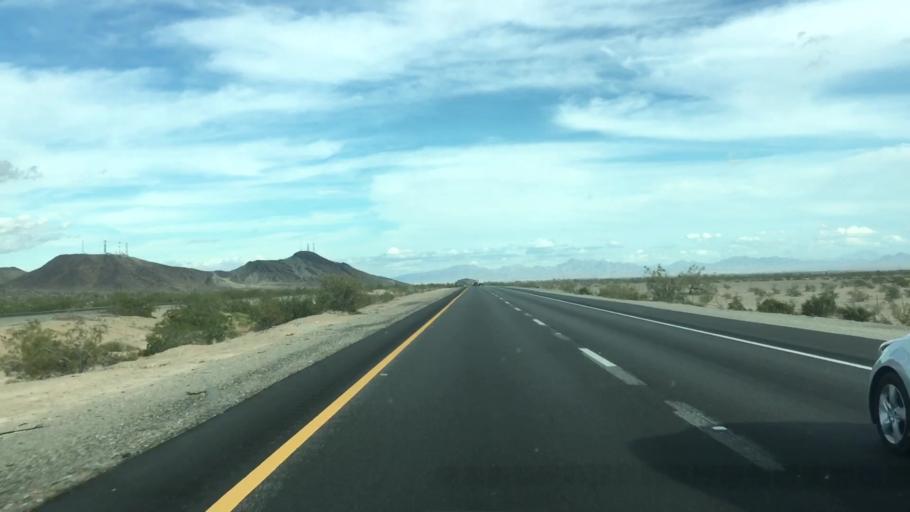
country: US
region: California
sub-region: Riverside County
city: Mesa Verde
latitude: 33.6098
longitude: -114.7963
